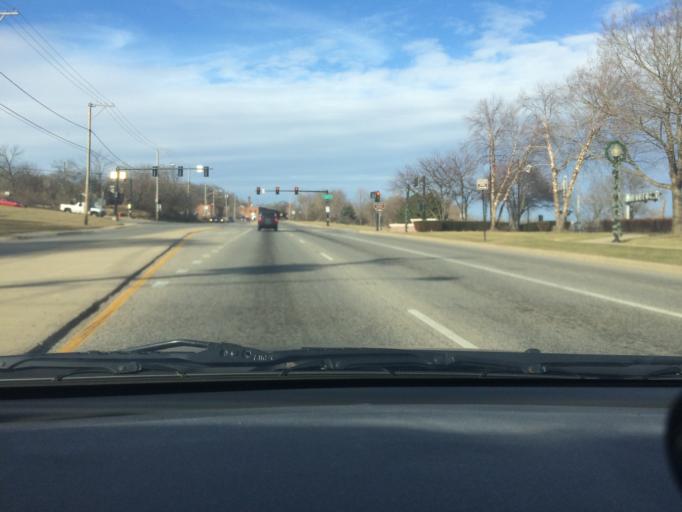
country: US
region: Illinois
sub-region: Kane County
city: Elgin
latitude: 42.0406
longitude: -88.2904
